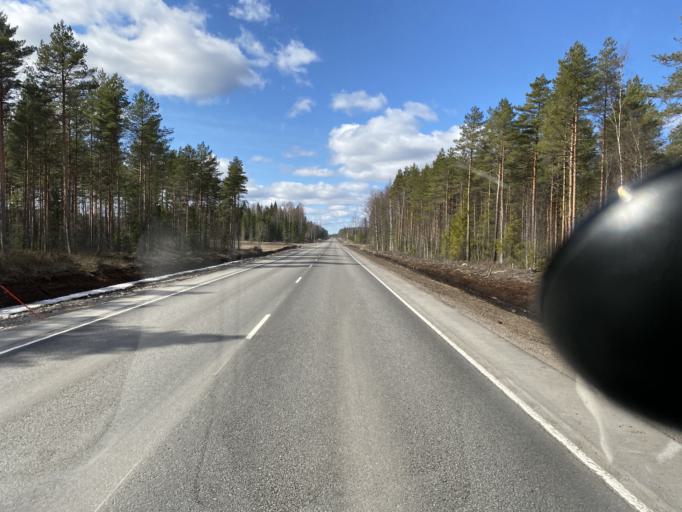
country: FI
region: Satakunta
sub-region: Pori
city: Huittinen
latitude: 61.1743
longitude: 22.5513
